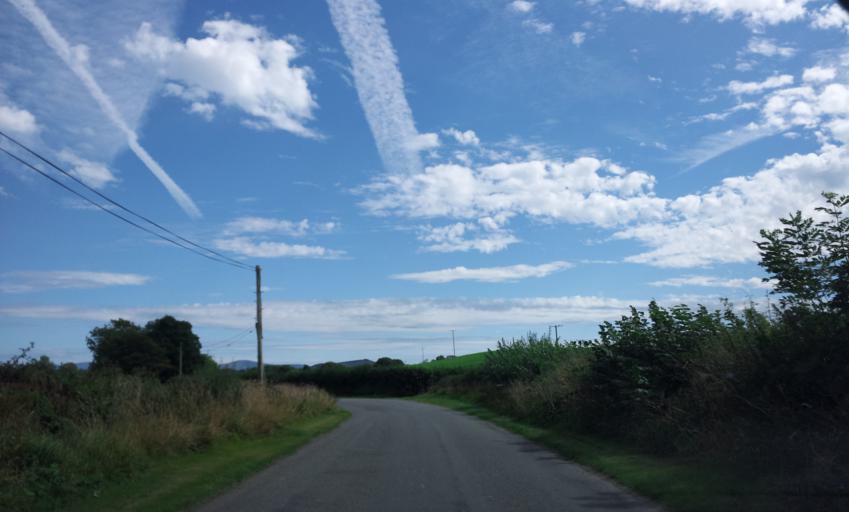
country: IE
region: Leinster
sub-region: Kildare
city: Moone
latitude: 52.9833
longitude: -6.8366
